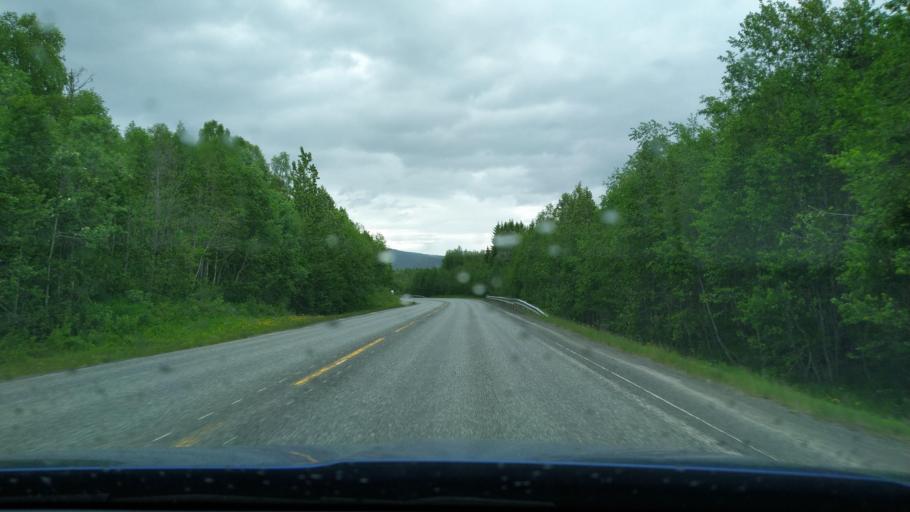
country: NO
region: Troms
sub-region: Malselv
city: Moen
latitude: 69.0722
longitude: 18.5364
